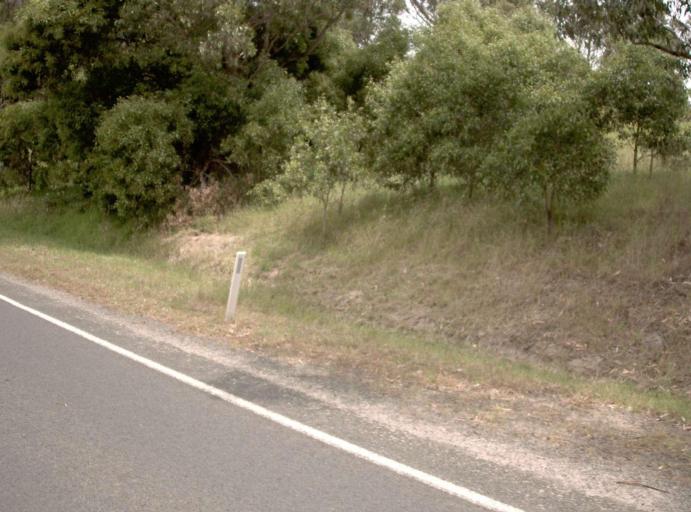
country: AU
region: Victoria
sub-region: Latrobe
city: Traralgon
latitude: -38.4638
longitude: 146.7197
